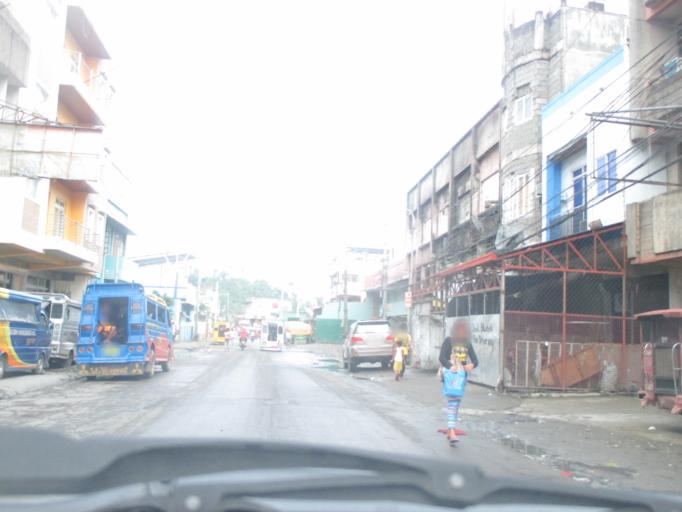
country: PH
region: Eastern Visayas
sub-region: Province of Leyte
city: Panalanoy
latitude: 11.2457
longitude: 124.9974
